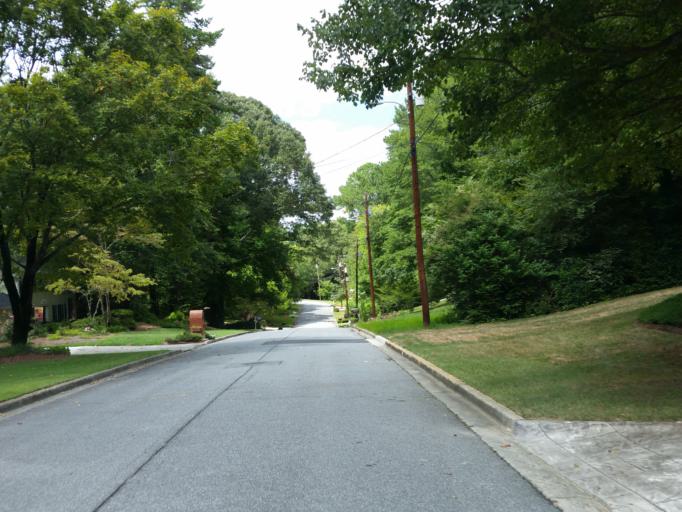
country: US
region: Georgia
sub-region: Cobb County
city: Smyrna
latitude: 33.9450
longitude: -84.4722
